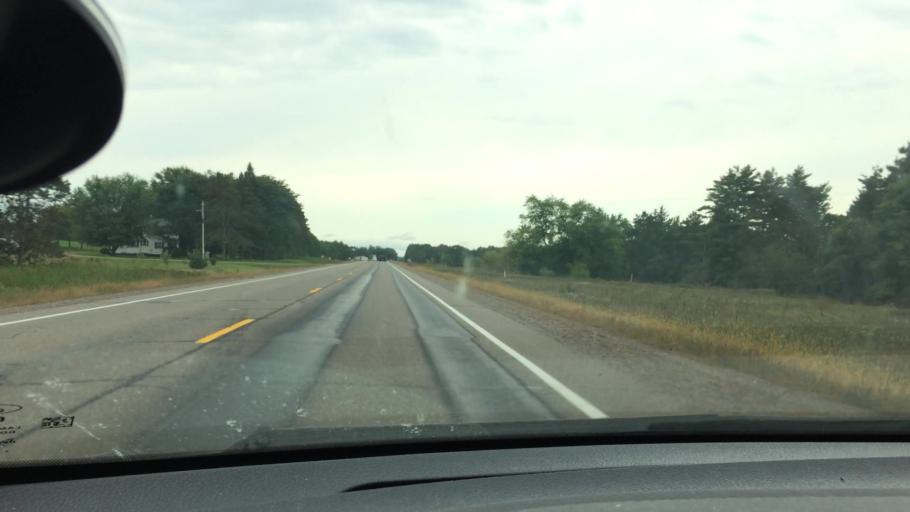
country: US
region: Wisconsin
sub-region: Eau Claire County
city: Augusta
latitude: 44.5844
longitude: -91.1055
